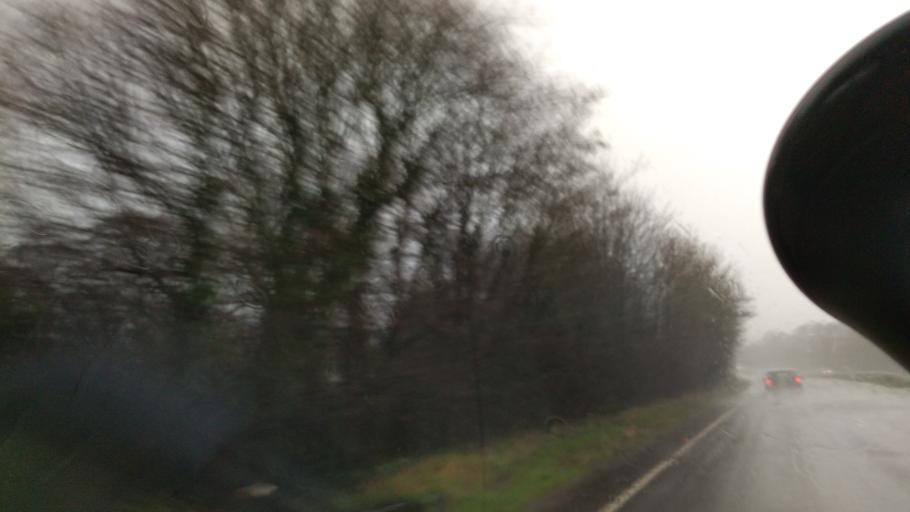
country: GB
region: England
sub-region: West Sussex
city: Walberton
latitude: 50.8532
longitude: -0.6286
